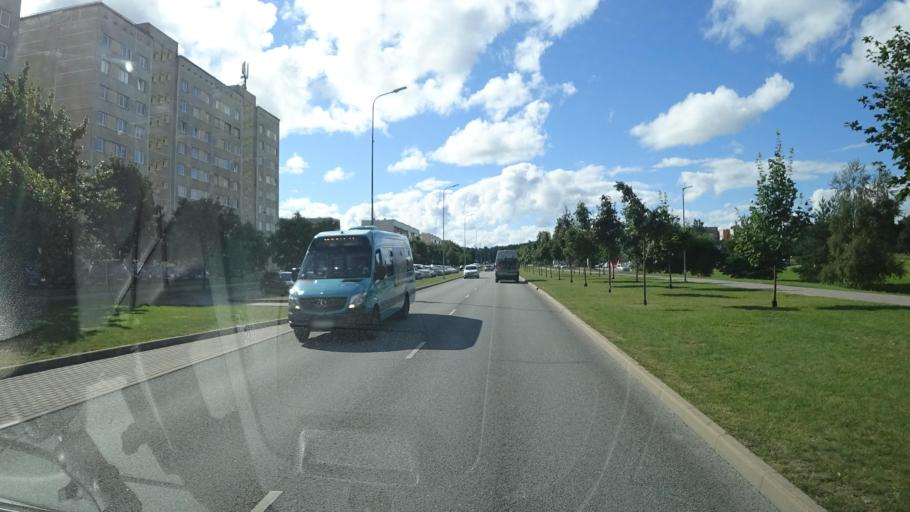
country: LV
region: Ventspils
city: Ventspils
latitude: 57.4068
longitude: 21.6017
